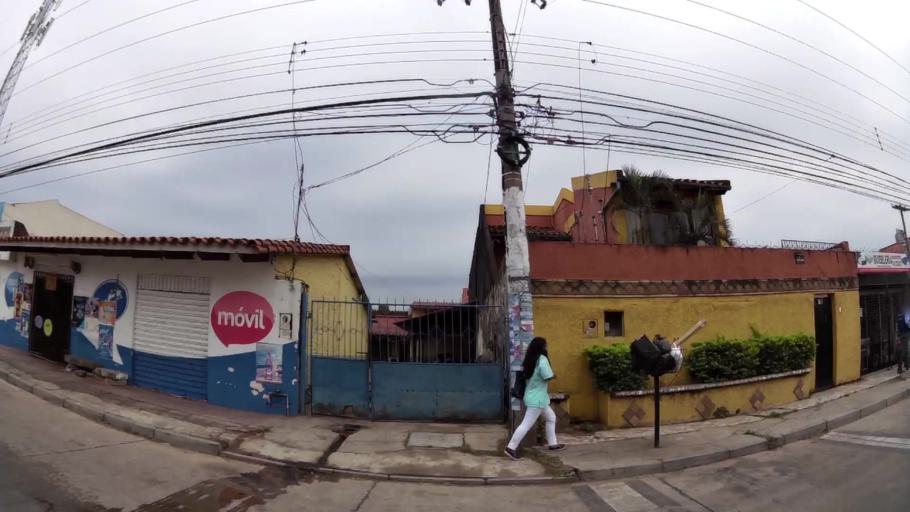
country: BO
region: Santa Cruz
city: Santa Cruz de la Sierra
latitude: -17.7725
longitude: -63.1562
